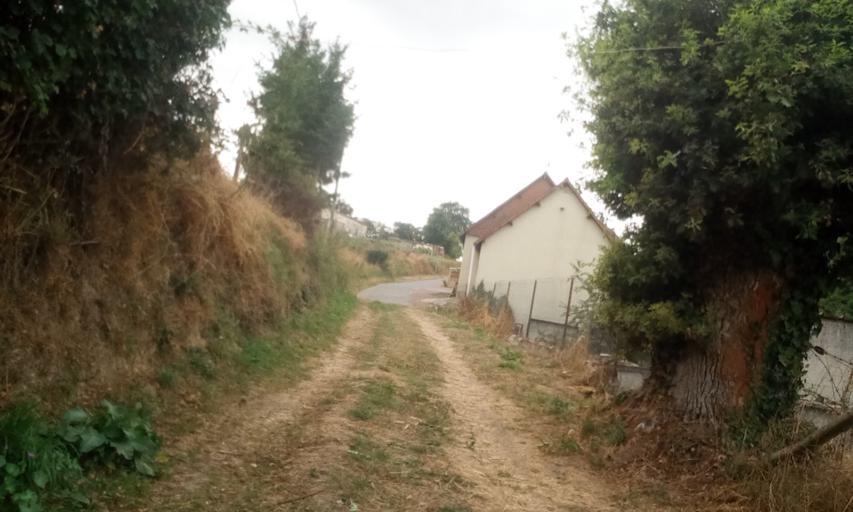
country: FR
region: Lower Normandy
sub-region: Departement du Calvados
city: Thury-Harcourt
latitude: 48.9860
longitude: -0.4299
